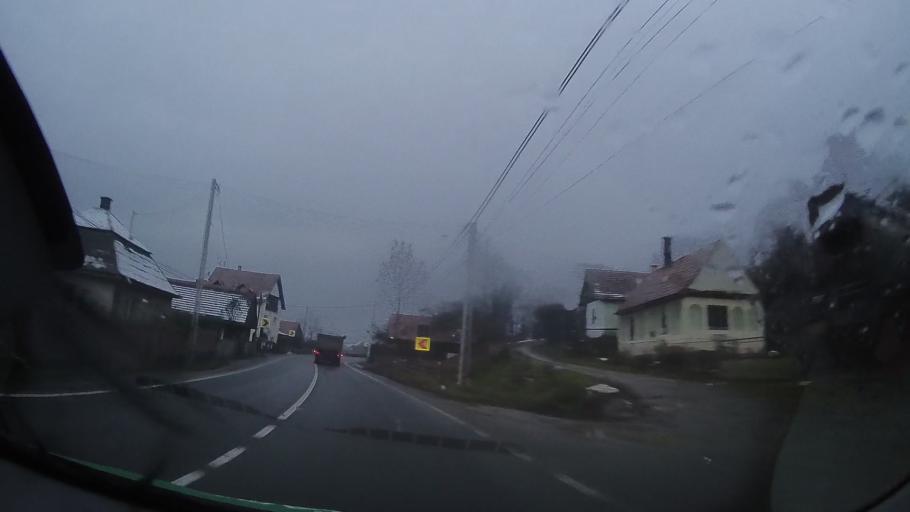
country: RO
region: Harghita
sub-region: Comuna Lazarea
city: Lazarea
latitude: 46.7523
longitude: 25.5199
